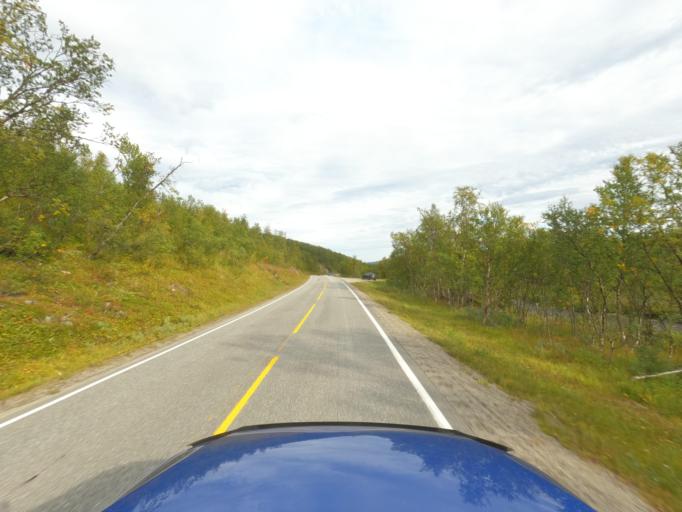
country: NO
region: Finnmark Fylke
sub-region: Porsanger
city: Lakselv
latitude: 70.4691
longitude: 24.9902
